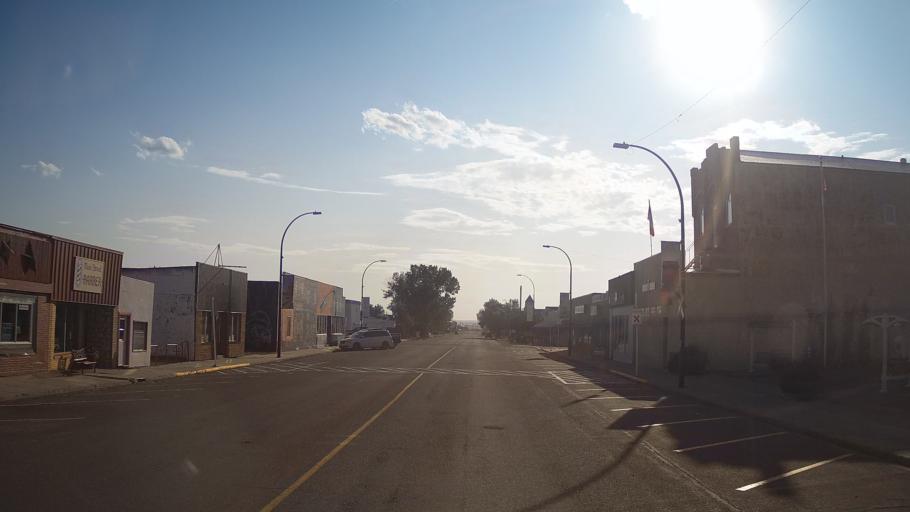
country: CA
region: Alberta
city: Hanna
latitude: 51.6422
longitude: -111.9308
